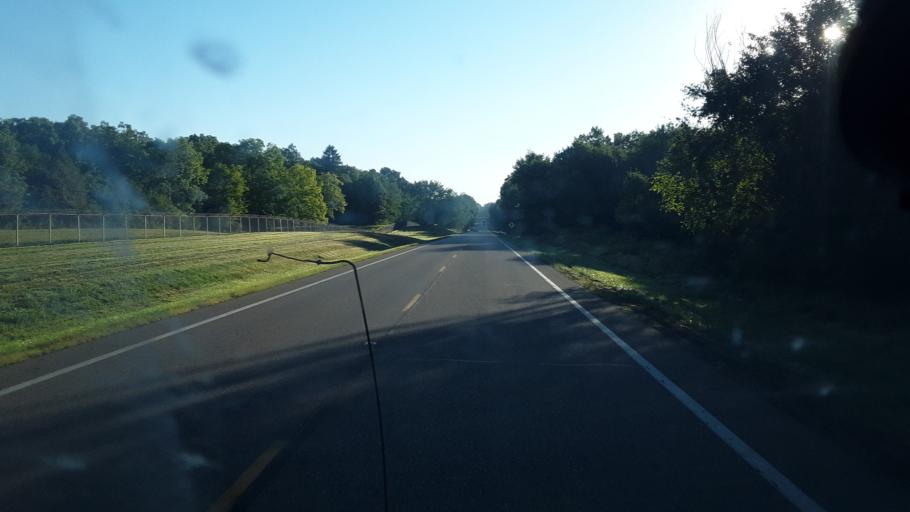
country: US
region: Ohio
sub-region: Trumbull County
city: South Canal
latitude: 41.1878
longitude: -81.0221
